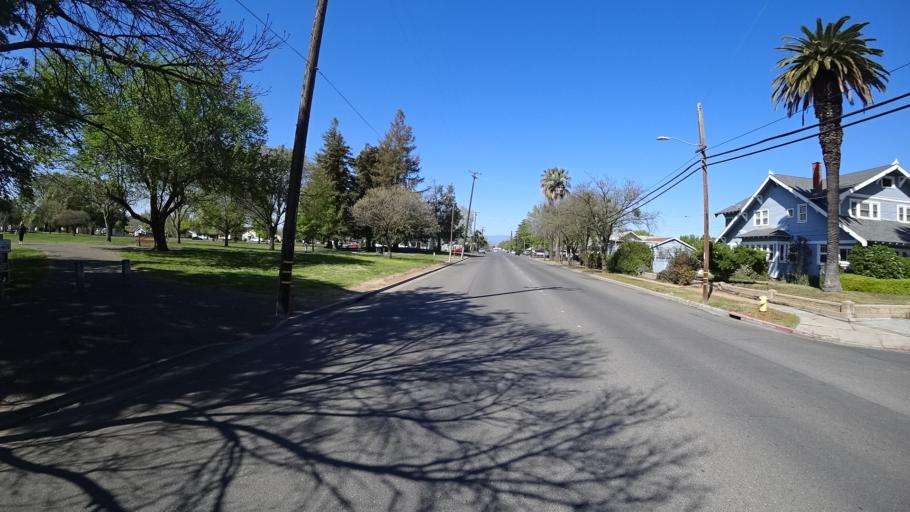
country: US
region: California
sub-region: Glenn County
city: Willows
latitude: 39.5205
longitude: -122.2032
